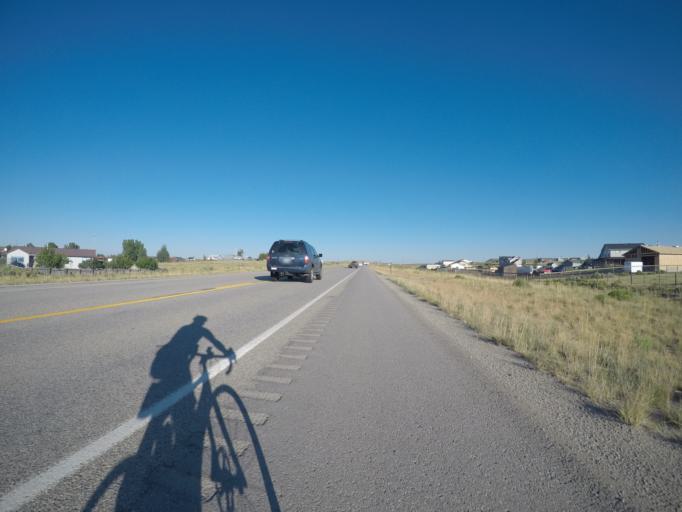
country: US
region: Wyoming
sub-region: Sublette County
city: Pinedale
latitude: 42.8800
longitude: -109.9699
